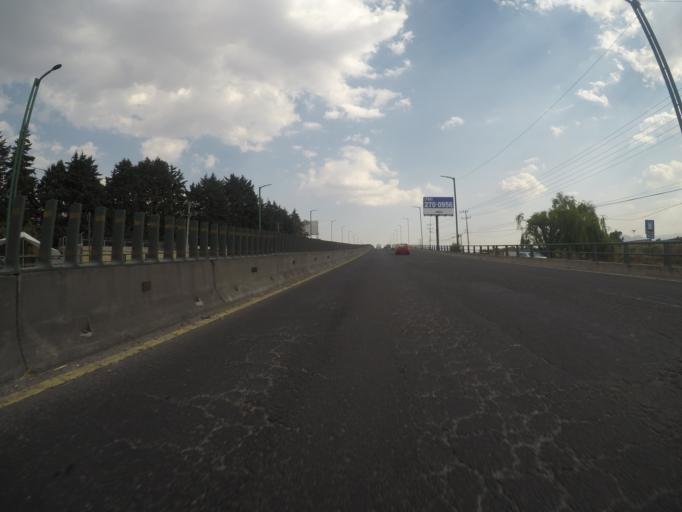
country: MX
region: Morelos
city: San Miguel Totocuitlapilco
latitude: 19.2378
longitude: -99.5988
